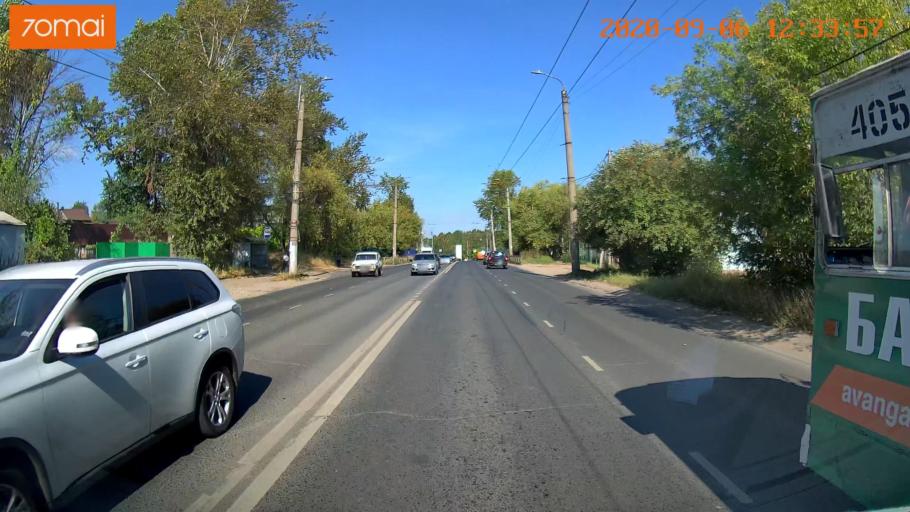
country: RU
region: Ivanovo
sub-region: Gorod Ivanovo
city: Ivanovo
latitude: 57.0149
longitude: 40.9999
